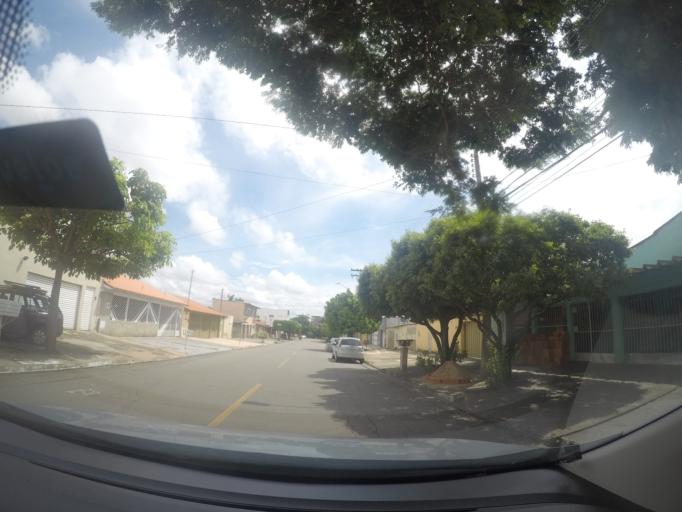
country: BR
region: Goias
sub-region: Goiania
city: Goiania
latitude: -16.7184
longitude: -49.3179
